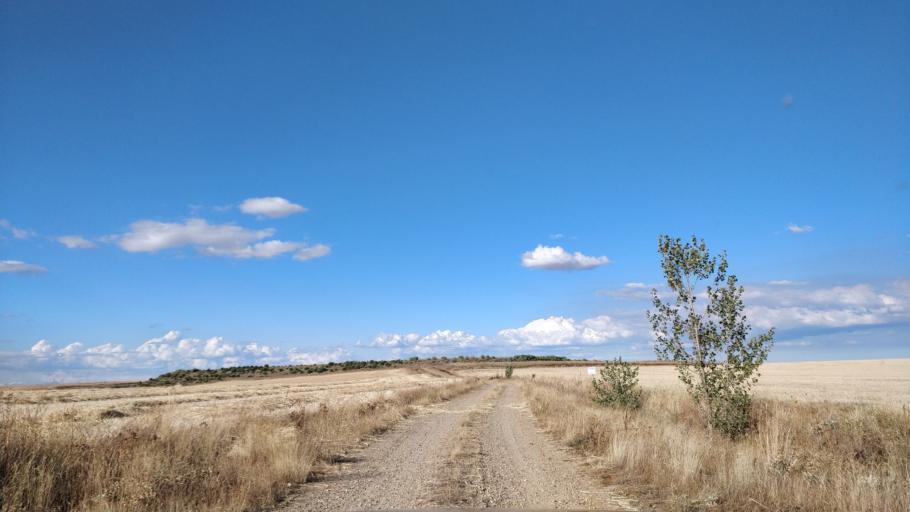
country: ES
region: Castille and Leon
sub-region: Provincia de Leon
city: Santa Cristina de Valmadrigal
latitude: 42.3424
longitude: -5.2705
